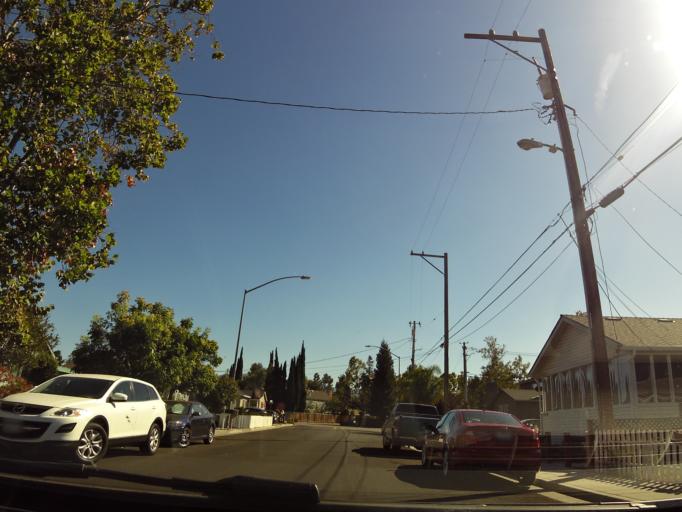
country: US
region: California
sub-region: Santa Clara County
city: Monte Sereno
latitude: 37.2659
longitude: -121.9778
